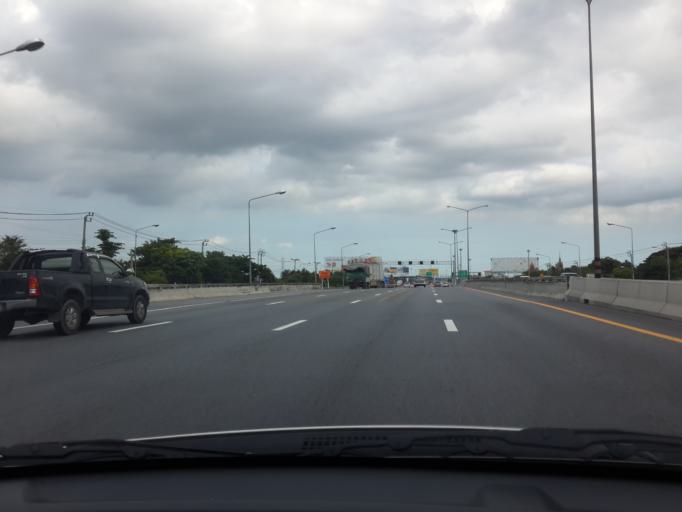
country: TH
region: Bangkok
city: Saphan Sung
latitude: 13.7608
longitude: 100.6966
